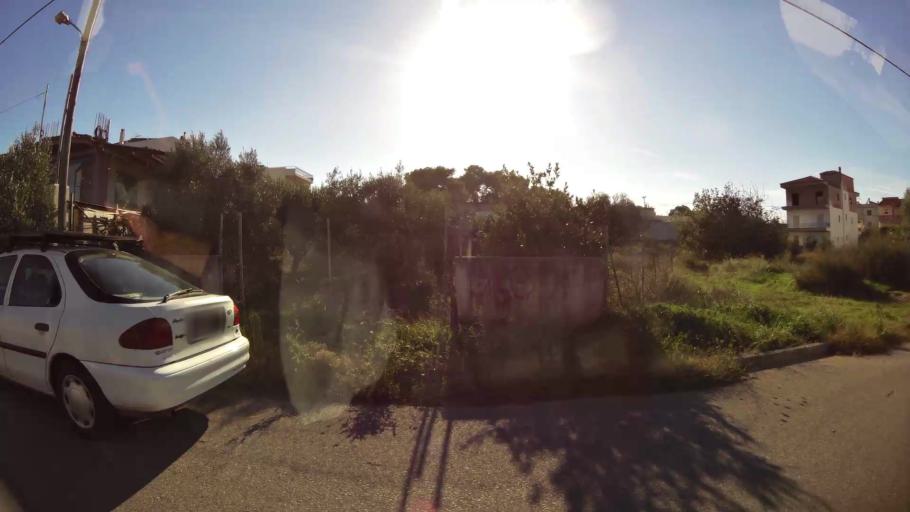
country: GR
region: Attica
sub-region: Nomarchia Anatolikis Attikis
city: Kalyvia Thorikou
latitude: 37.8417
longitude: 23.9325
